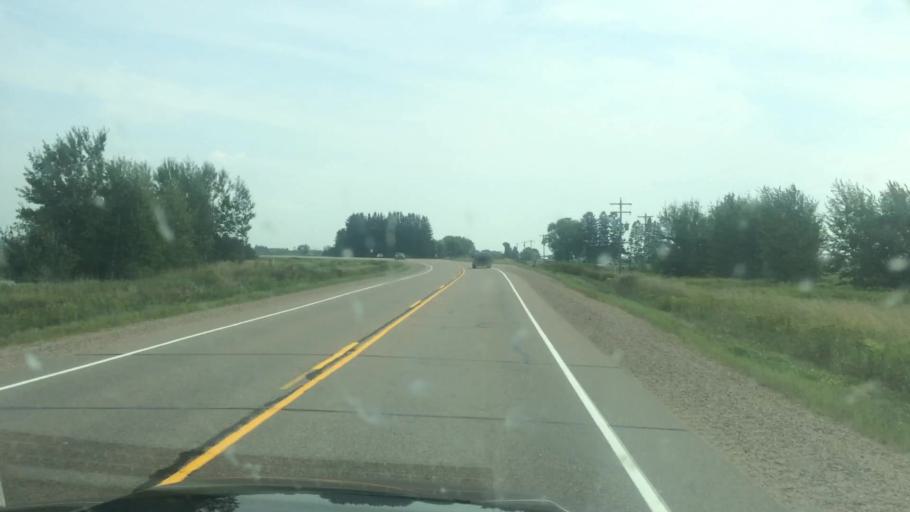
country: US
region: Wisconsin
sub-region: Langlade County
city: Antigo
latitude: 45.1401
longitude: -89.1959
